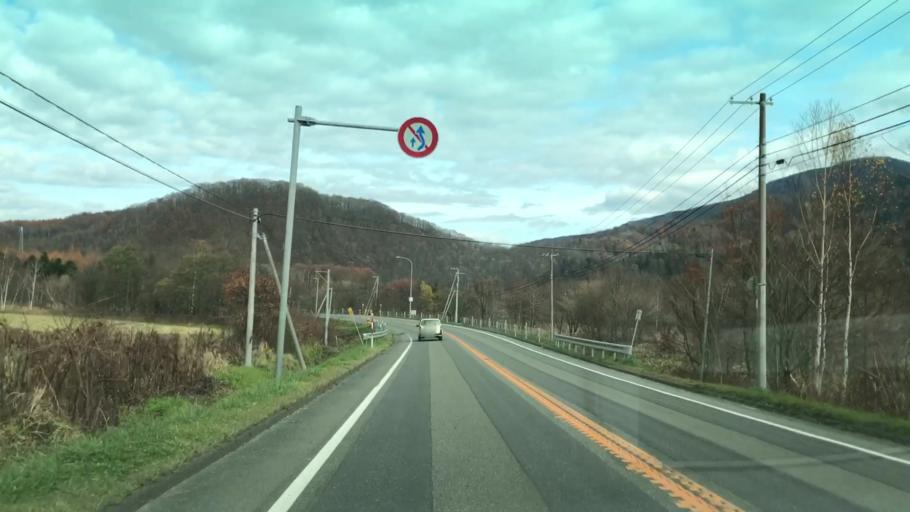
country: JP
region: Hokkaido
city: Shizunai-furukawacho
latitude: 42.7831
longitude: 142.3938
